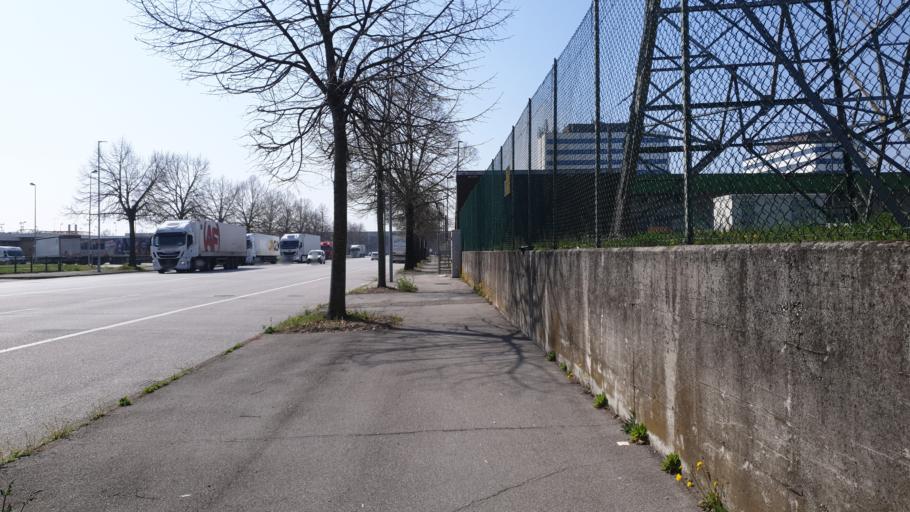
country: IT
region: Veneto
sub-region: Provincia di Padova
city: Ponte San Nicolo
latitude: 45.3904
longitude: 11.9301
